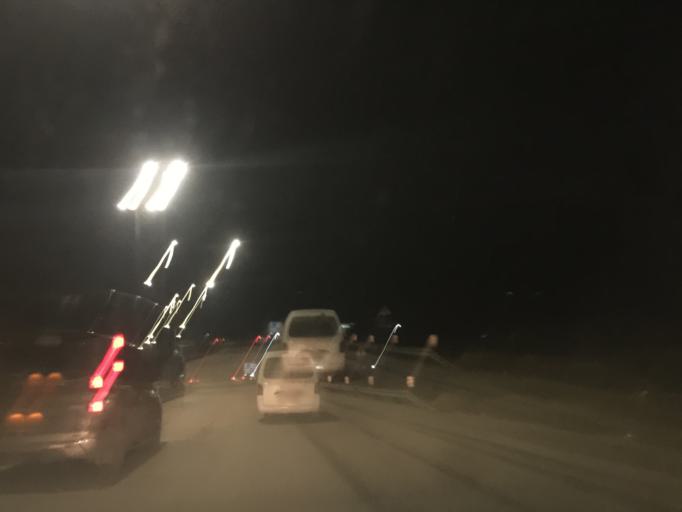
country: JO
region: Zarqa
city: Russeifa
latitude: 32.0211
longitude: 35.9881
